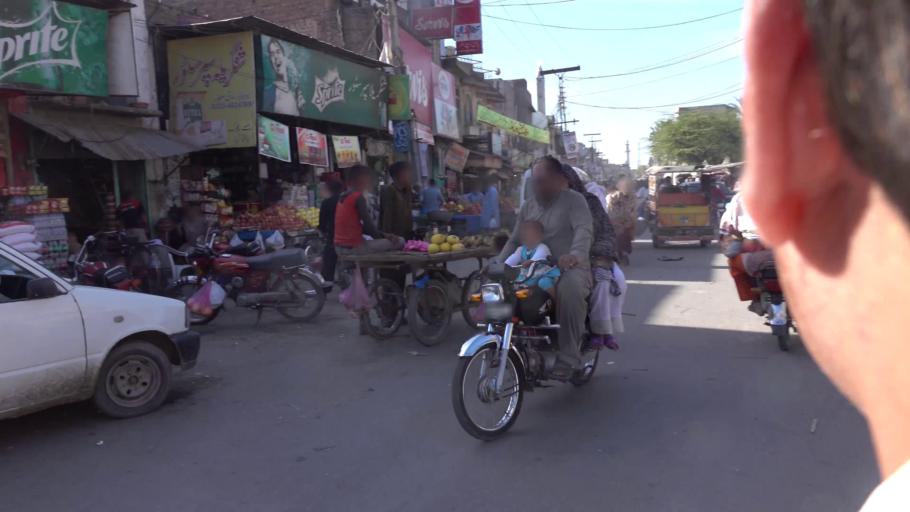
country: PK
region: Punjab
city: Hafizabad
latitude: 32.0724
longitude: 73.6872
